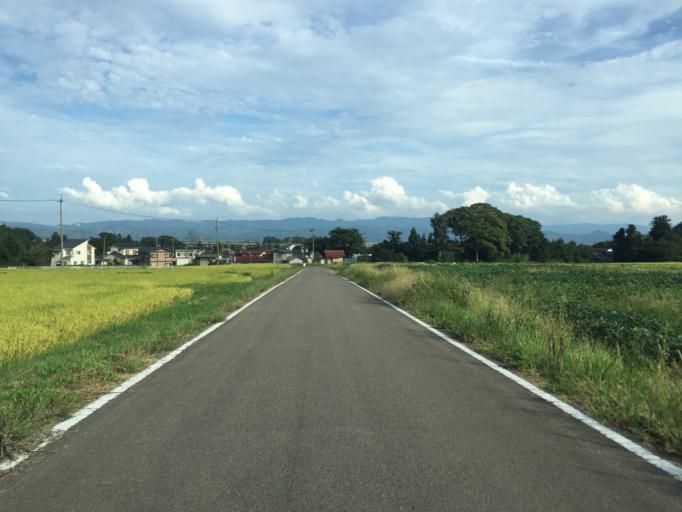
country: JP
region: Fukushima
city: Hobaramachi
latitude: 37.8841
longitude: 140.5293
